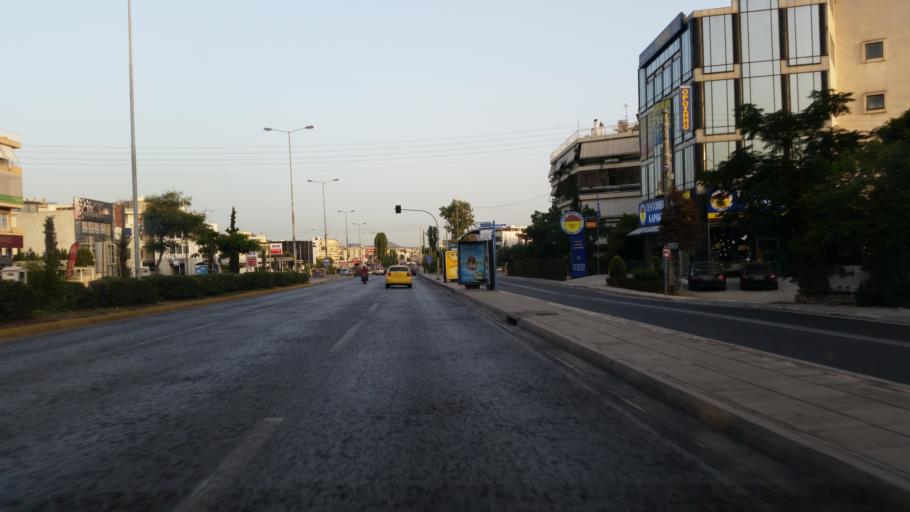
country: GR
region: Attica
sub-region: Nomarchia Athinas
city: Glyfada
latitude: 37.8776
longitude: 23.7553
